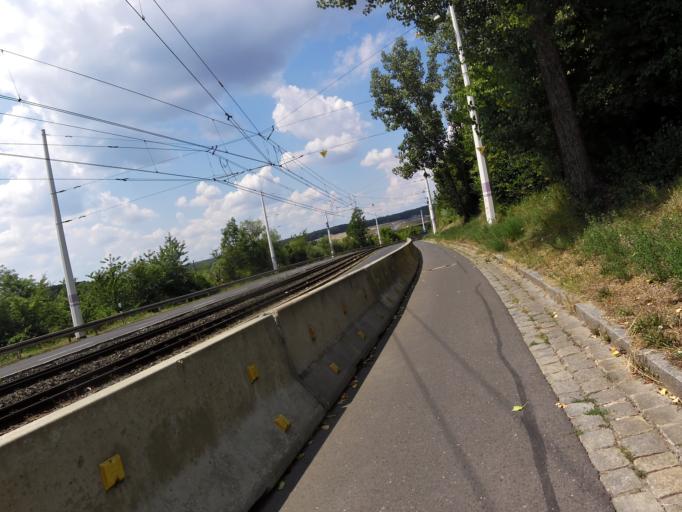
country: DE
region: Bavaria
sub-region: Regierungsbezirk Unterfranken
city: Randersacker
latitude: 49.7510
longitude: 9.9492
